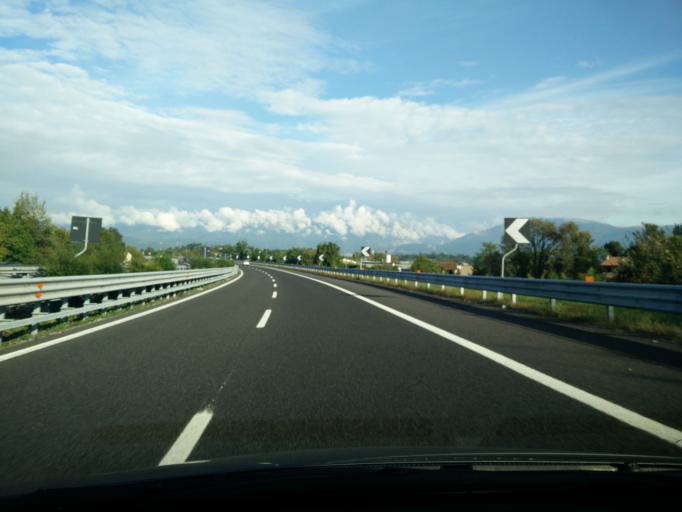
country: IT
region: Veneto
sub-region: Provincia di Treviso
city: San Martino
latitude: 45.9053
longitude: 12.3445
